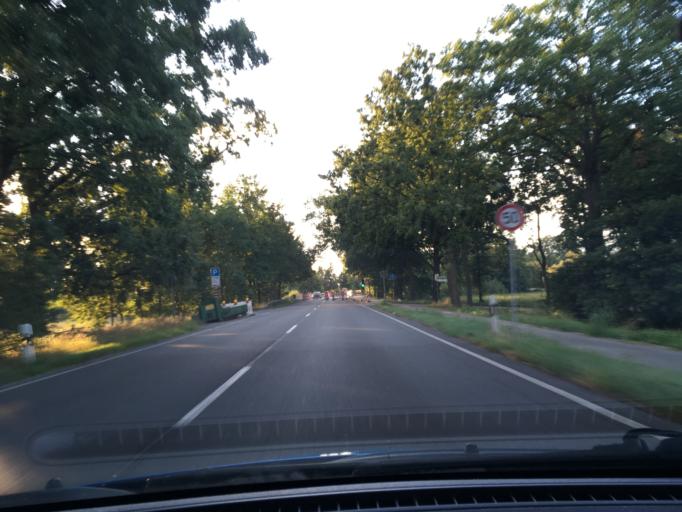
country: DE
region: Lower Saxony
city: Hambuhren
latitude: 52.6933
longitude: 9.9859
